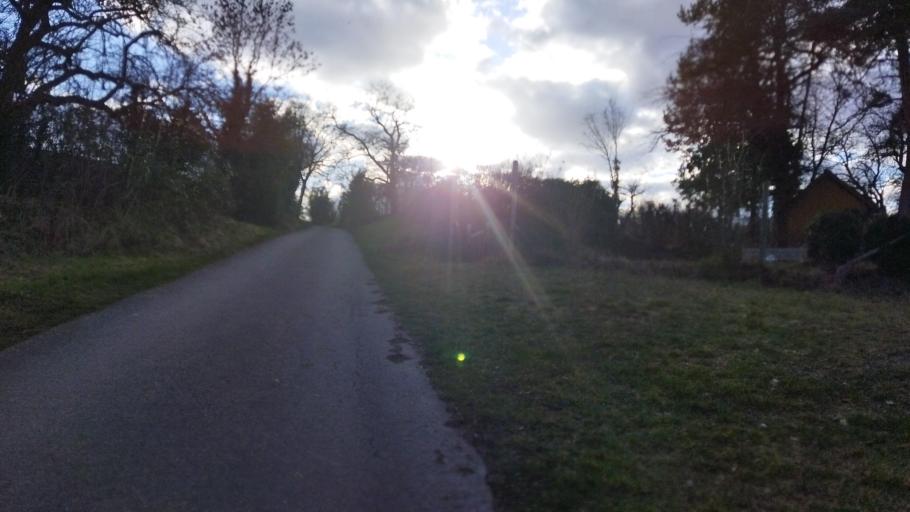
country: DE
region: Baden-Wuerttemberg
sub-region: Regierungsbezirk Stuttgart
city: Guglingen
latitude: 49.0743
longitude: 9.0033
